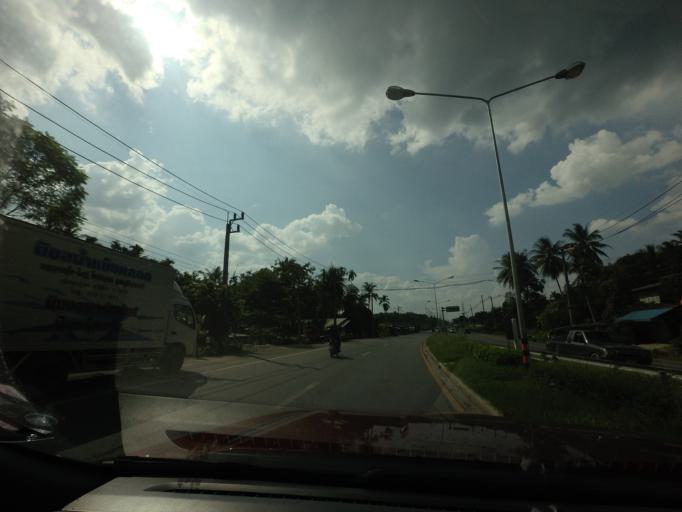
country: TH
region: Yala
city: Krong Pi Nang
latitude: 6.4742
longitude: 101.2658
